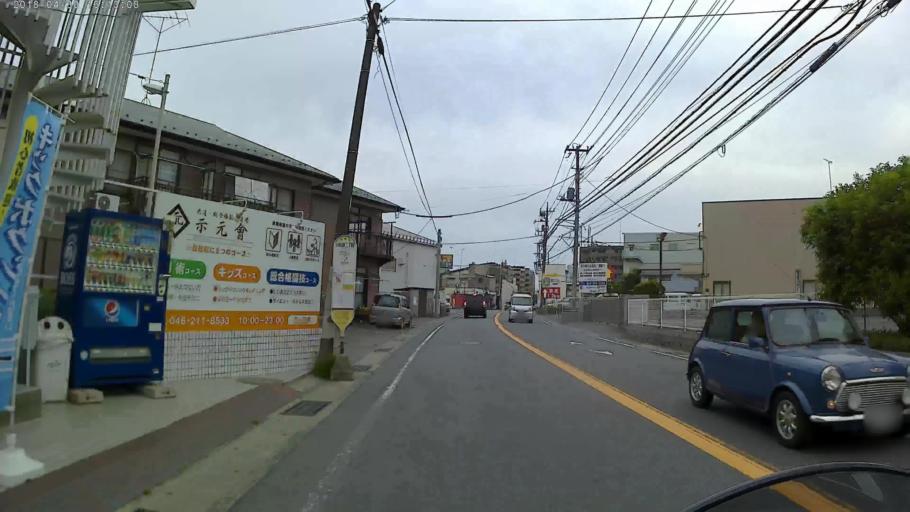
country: JP
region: Kanagawa
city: Minami-rinkan
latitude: 35.4915
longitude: 139.4313
